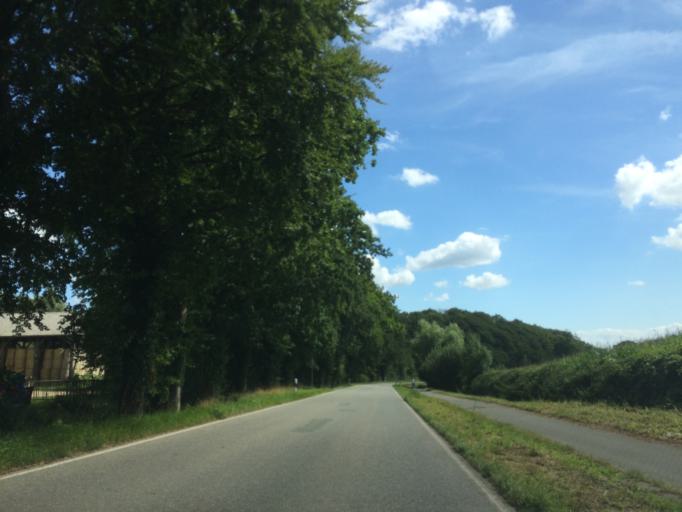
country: DE
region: Schleswig-Holstein
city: Grebin
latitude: 54.1895
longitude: 10.5242
